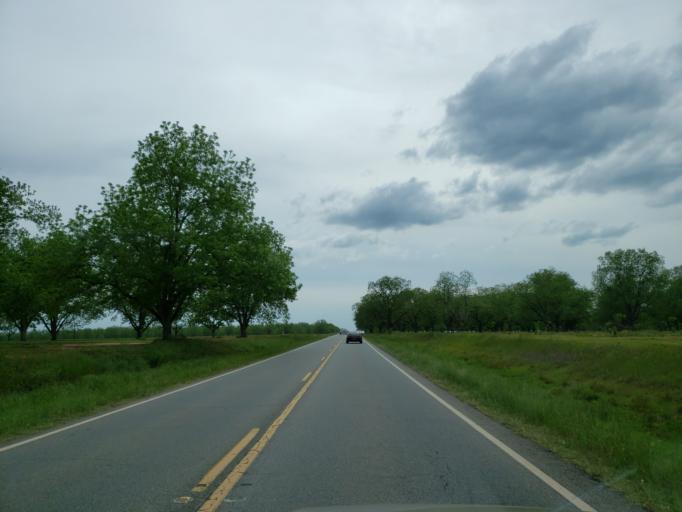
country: US
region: Georgia
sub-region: Houston County
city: Perry
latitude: 32.4372
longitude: -83.7967
